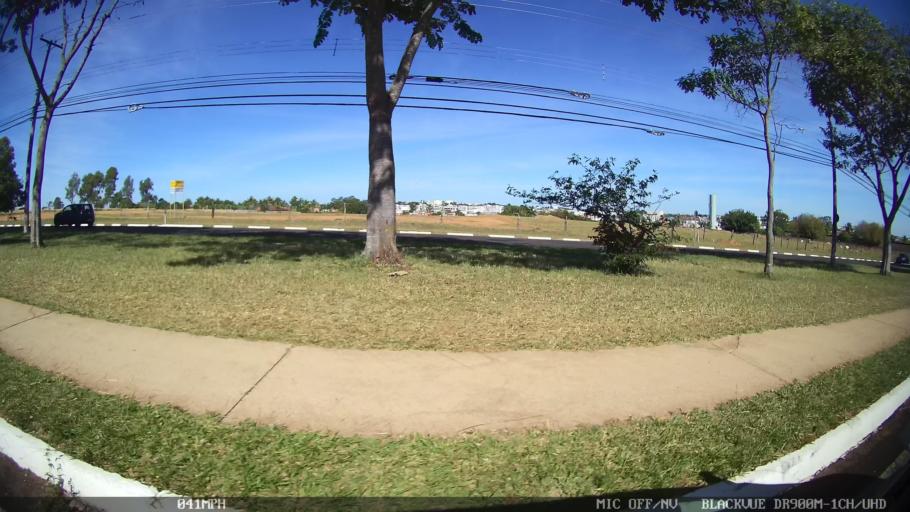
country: BR
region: Sao Paulo
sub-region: Franca
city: Franca
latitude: -20.5572
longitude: -47.3824
